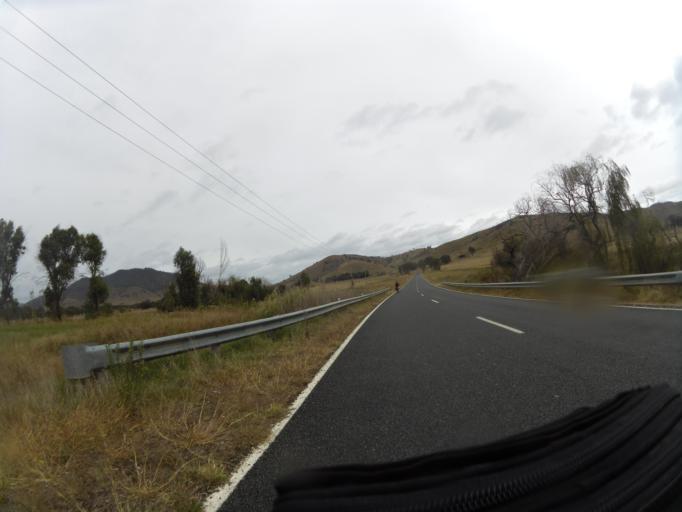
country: AU
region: New South Wales
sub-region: Greater Hume Shire
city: Holbrook
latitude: -36.2053
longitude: 147.7427
